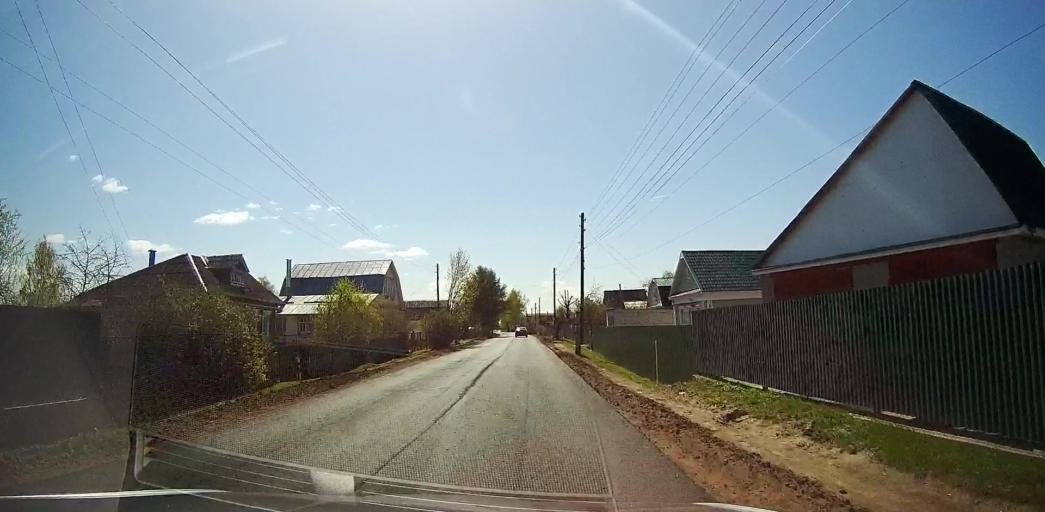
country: RU
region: Moskovskaya
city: Malyshevo
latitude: 55.4760
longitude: 38.3964
